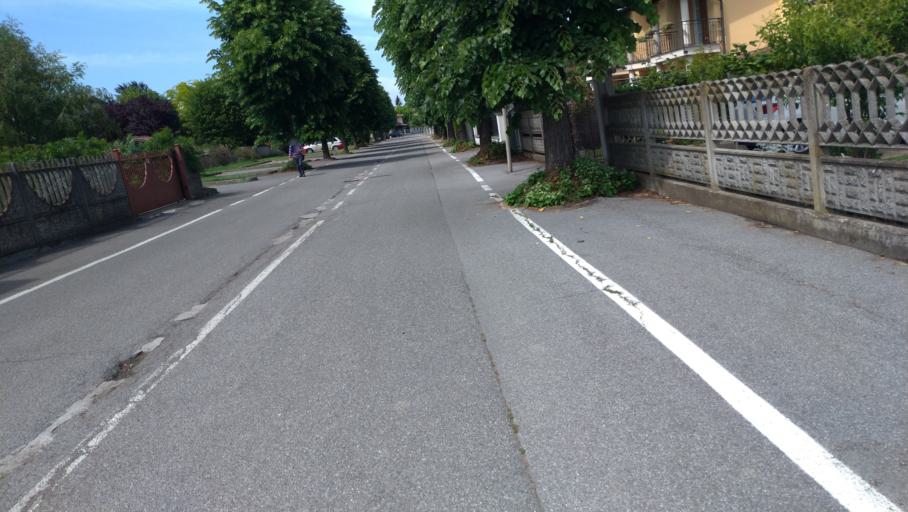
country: IT
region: Lombardy
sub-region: Provincia di Cremona
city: Madignano
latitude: 45.3431
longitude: 9.7220
